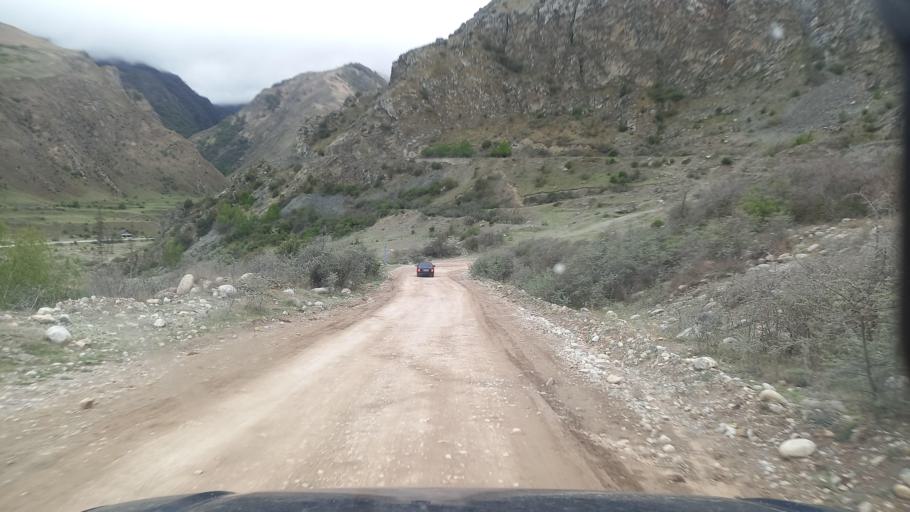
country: RU
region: Kabardino-Balkariya
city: Bylym
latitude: 43.4581
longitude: 43.0087
